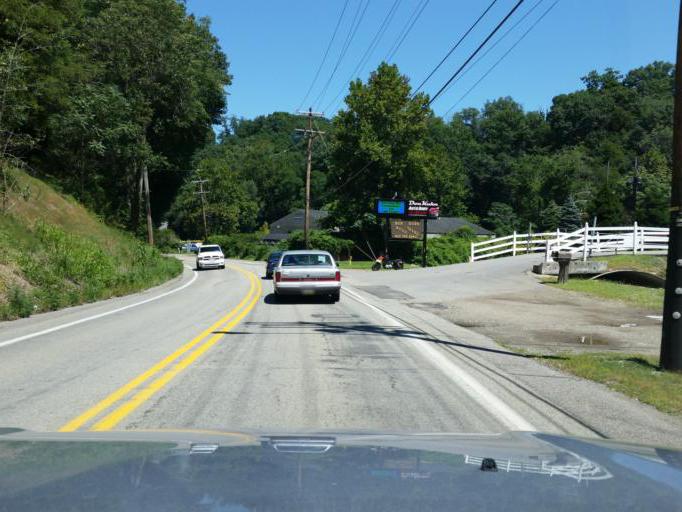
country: US
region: Pennsylvania
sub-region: Allegheny County
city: Blawnox
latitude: 40.4775
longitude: -79.8480
